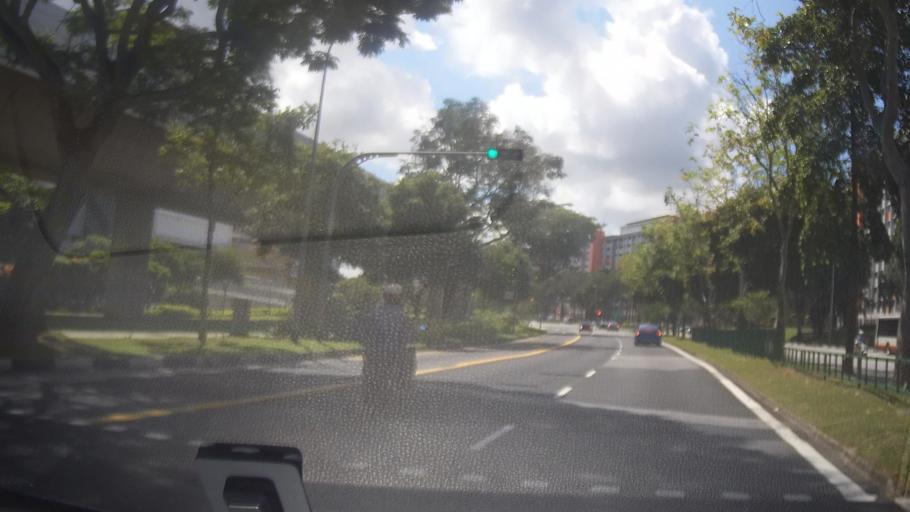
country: MY
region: Johor
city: Johor Bahru
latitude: 1.4315
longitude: 103.7779
